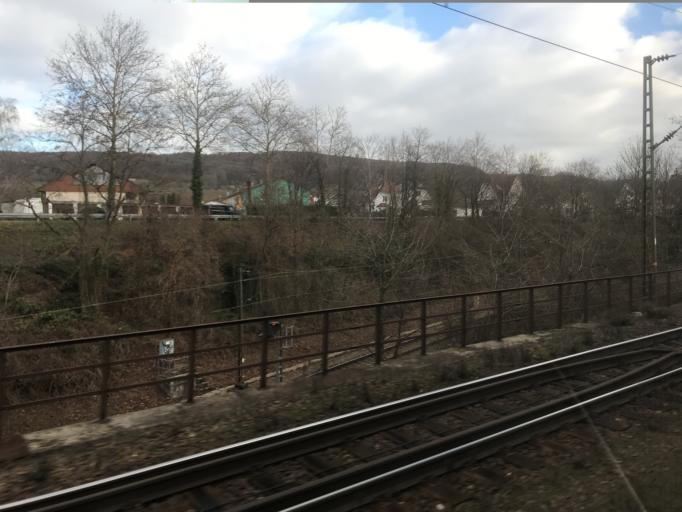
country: DE
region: Baden-Wuerttemberg
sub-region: Freiburg Region
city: Weil am Rhein
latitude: 47.6107
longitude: 7.6141
